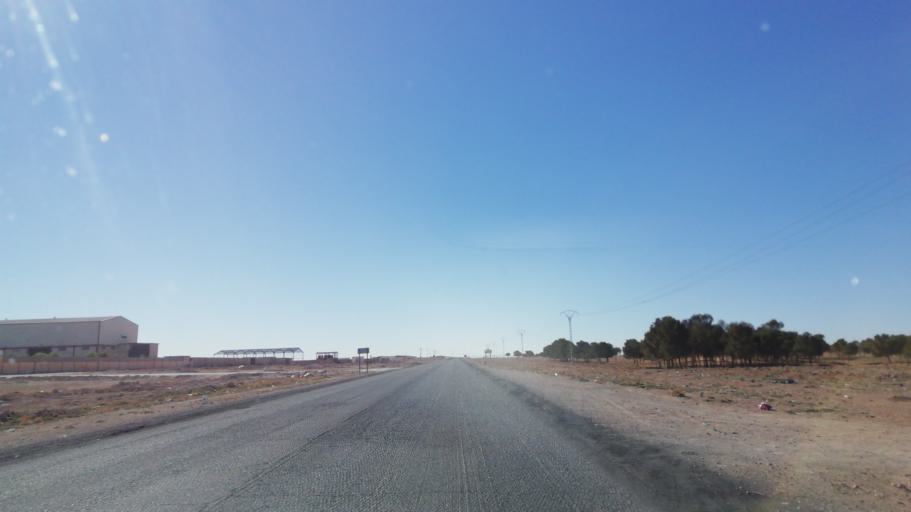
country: DZ
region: Saida
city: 'Ain el Hadjar
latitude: 34.0307
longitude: 0.0734
